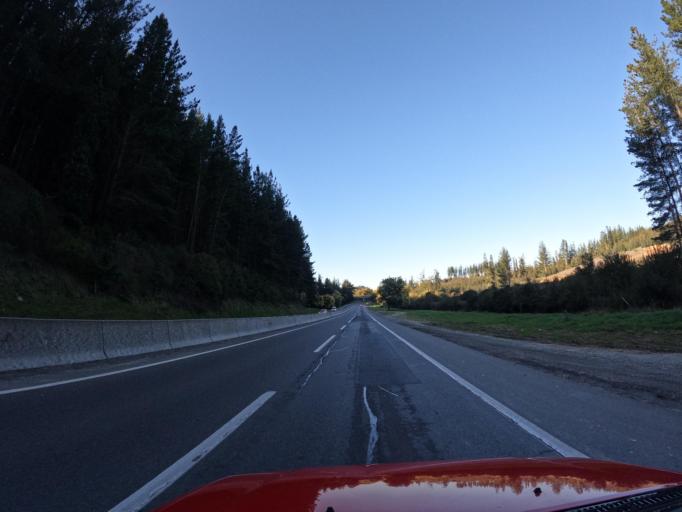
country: CL
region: Biobio
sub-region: Provincia de Concepcion
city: Penco
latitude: -36.7281
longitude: -72.8410
